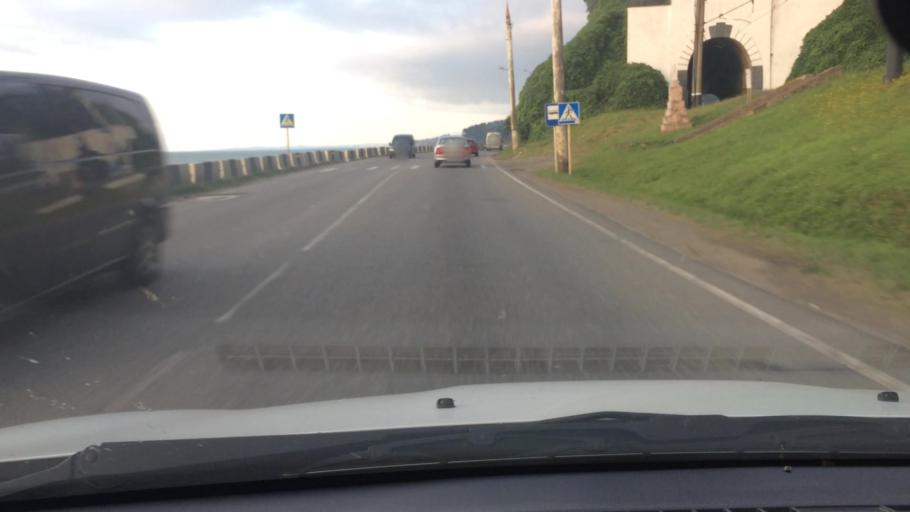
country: GE
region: Ajaria
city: Makhinjauri
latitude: 41.6703
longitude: 41.6884
